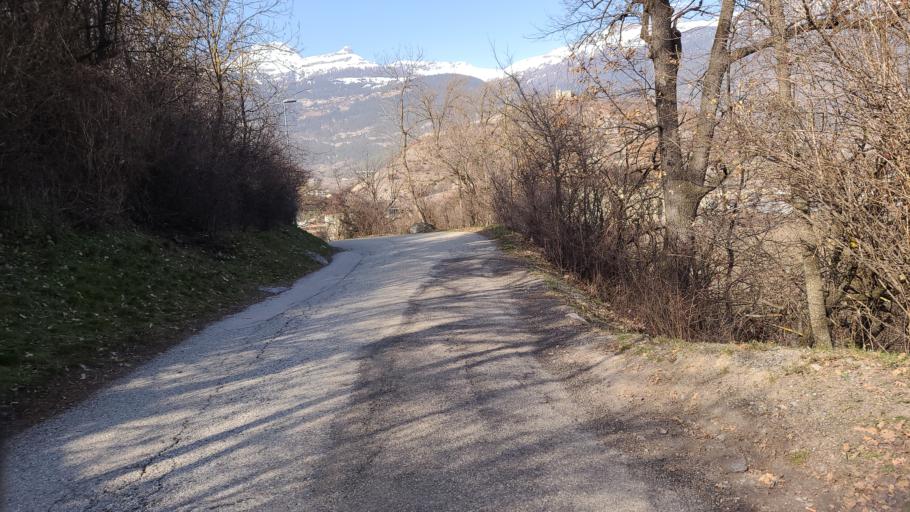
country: CH
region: Valais
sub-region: Sierre District
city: Sierre
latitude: 46.2944
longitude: 7.5451
